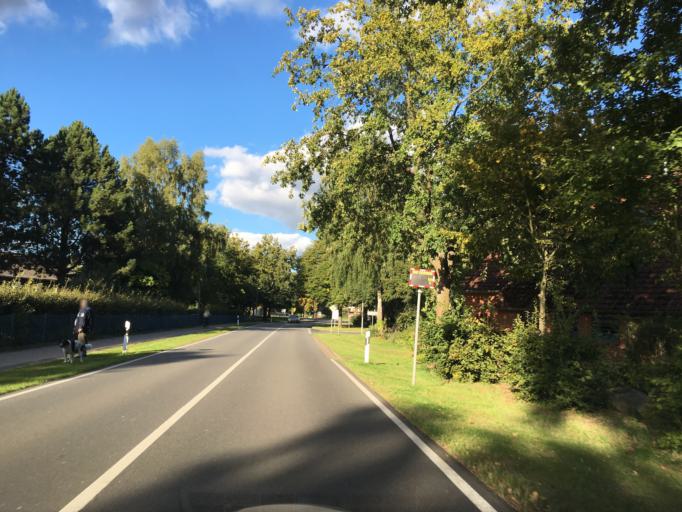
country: DE
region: Lower Saxony
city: Reppenstedt
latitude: 53.2465
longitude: 10.3519
